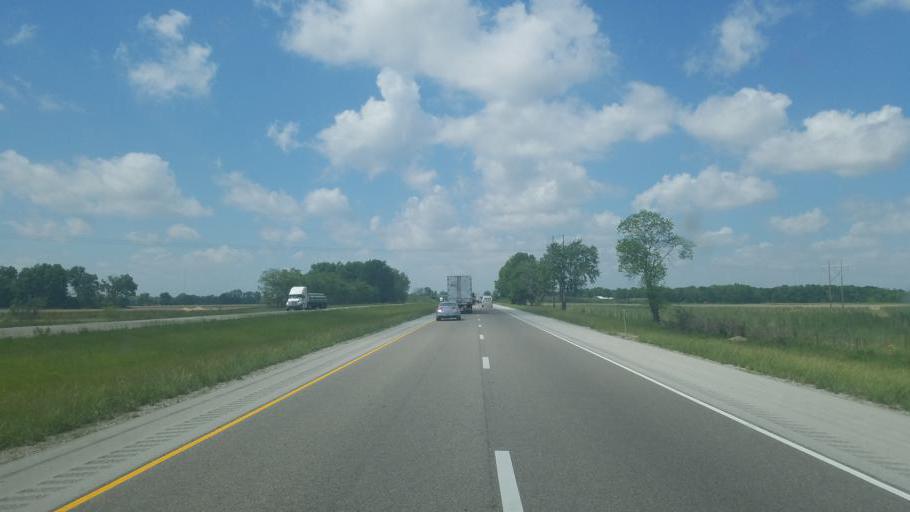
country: US
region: Illinois
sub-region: Cumberland County
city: Greenup
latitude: 39.2320
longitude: -88.2125
